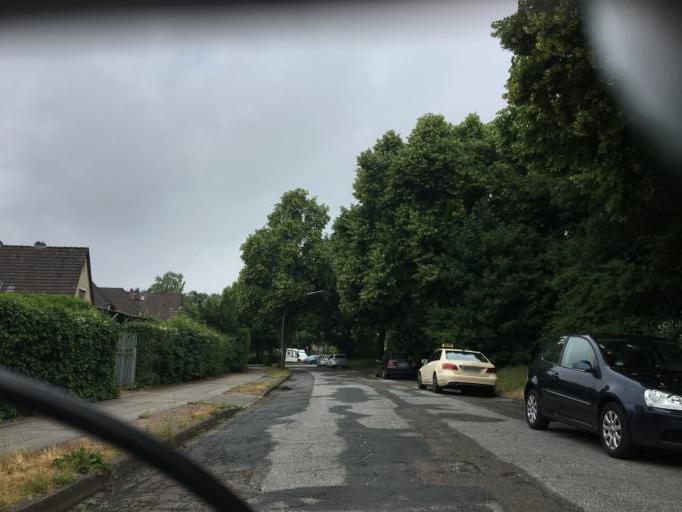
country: DE
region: Hamburg
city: Eidelstedt
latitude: 53.5779
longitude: 9.8658
